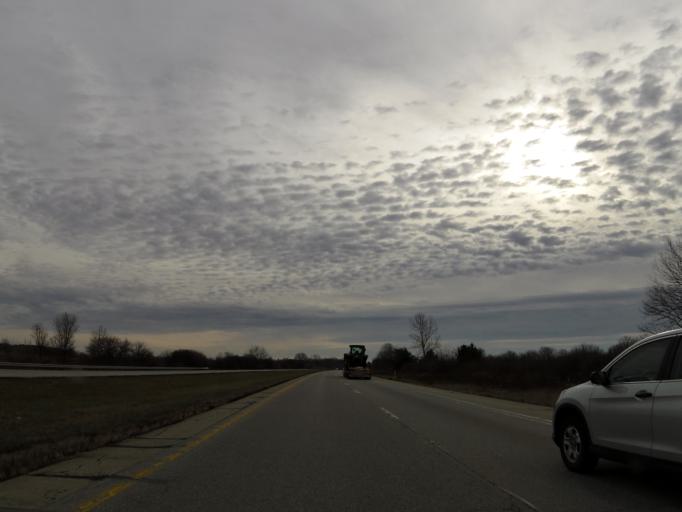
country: US
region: Indiana
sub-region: Hendricks County
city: Pittsboro
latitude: 39.9364
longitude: -86.6049
